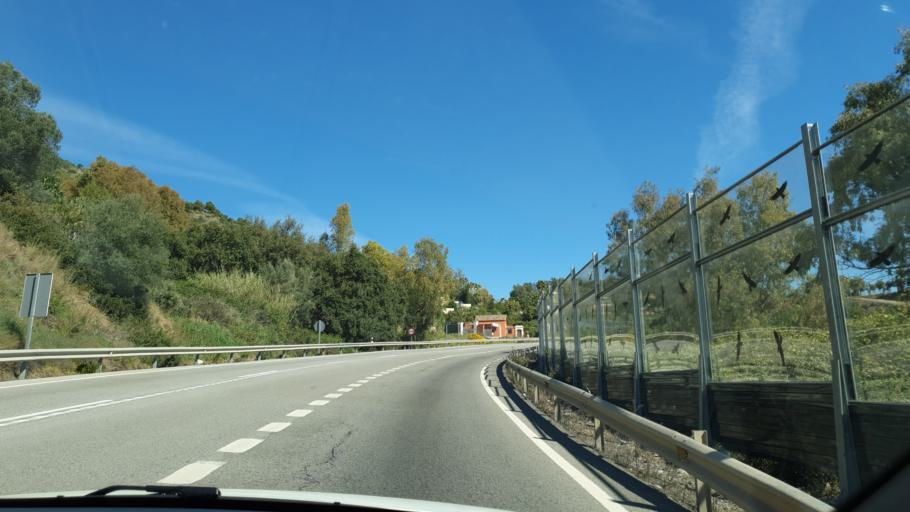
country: ES
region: Andalusia
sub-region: Provincia de Malaga
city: Ojen
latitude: 36.5427
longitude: -4.8643
